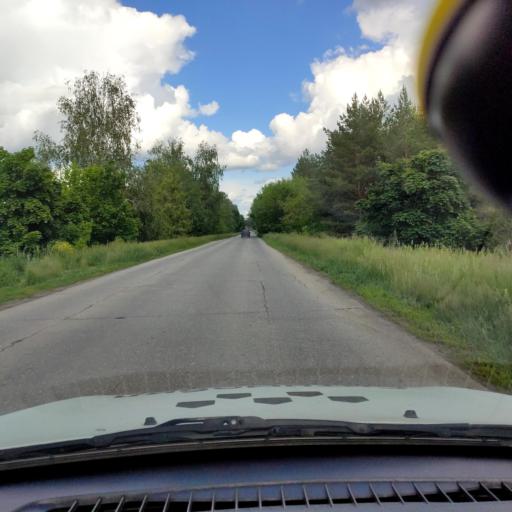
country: RU
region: Samara
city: Povolzhskiy
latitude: 53.6452
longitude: 49.7744
